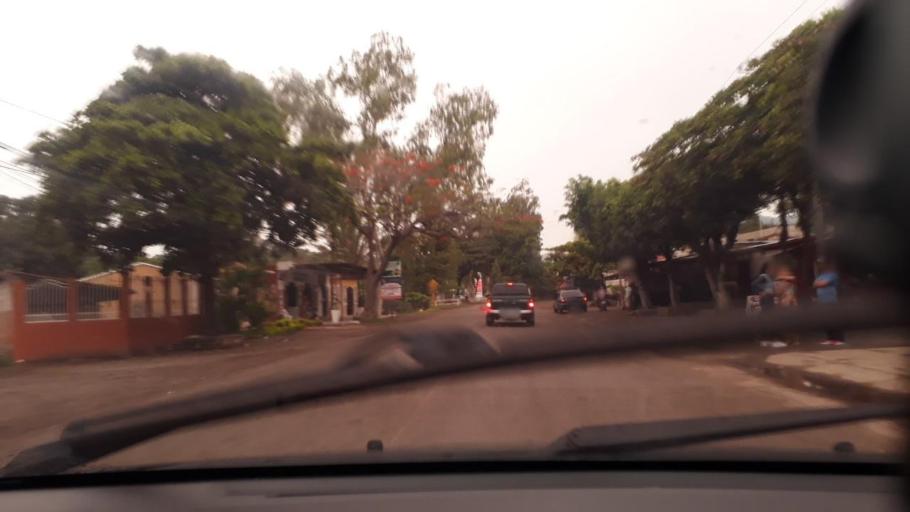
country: GT
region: Jutiapa
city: Asuncion Mita
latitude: 14.2835
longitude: -89.7260
